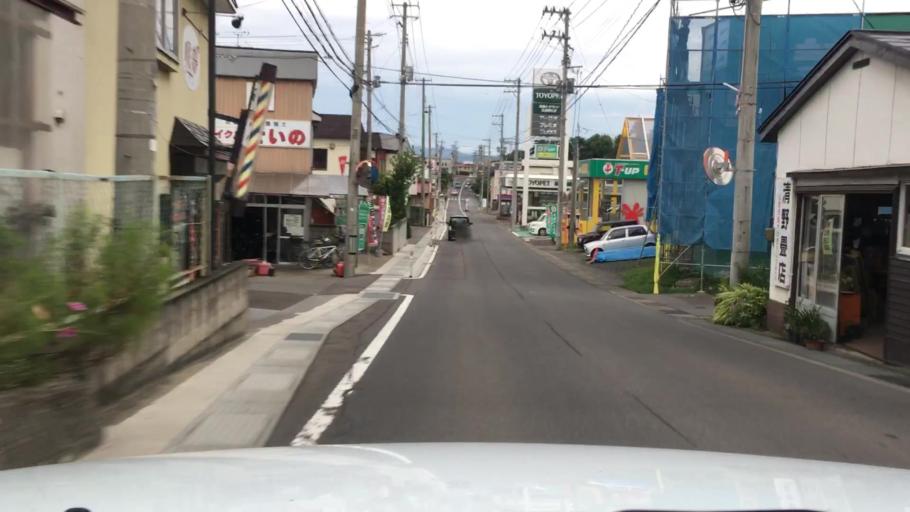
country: JP
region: Aomori
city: Hirosaki
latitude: 40.5864
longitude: 140.4641
